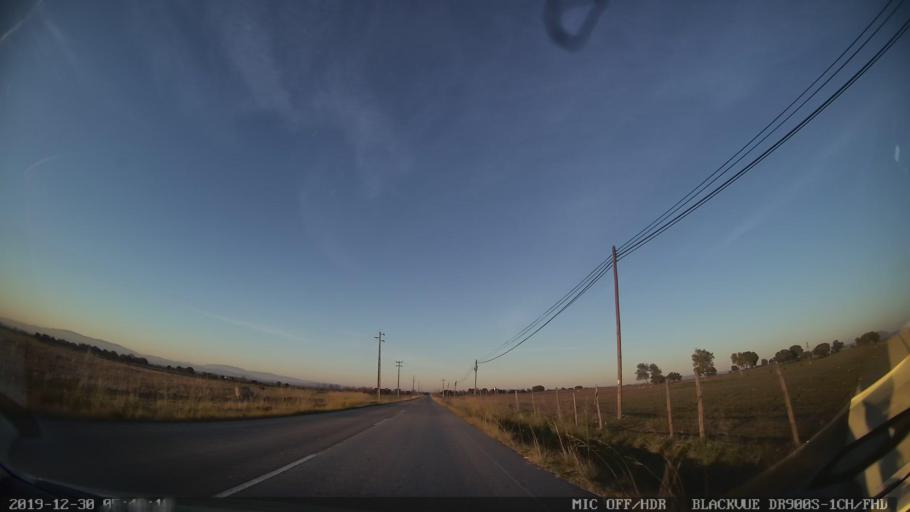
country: PT
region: Castelo Branco
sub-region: Idanha-A-Nova
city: Idanha-a-Nova
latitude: 39.9606
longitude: -7.2423
